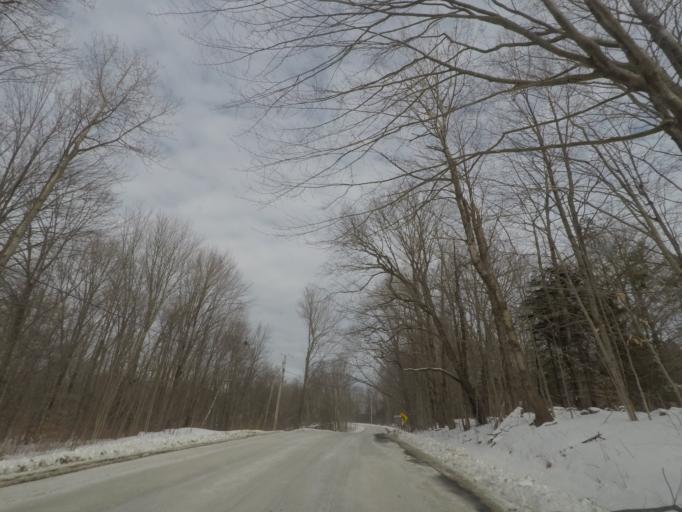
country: US
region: New York
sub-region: Rensselaer County
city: Averill Park
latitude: 42.5983
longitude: -73.4820
